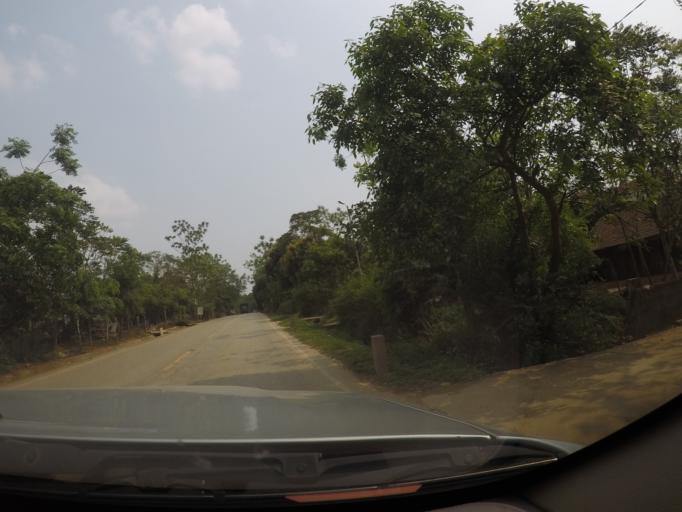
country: VN
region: Thanh Hoa
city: Thi Tran Yen Cat
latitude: 19.4802
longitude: 105.3965
